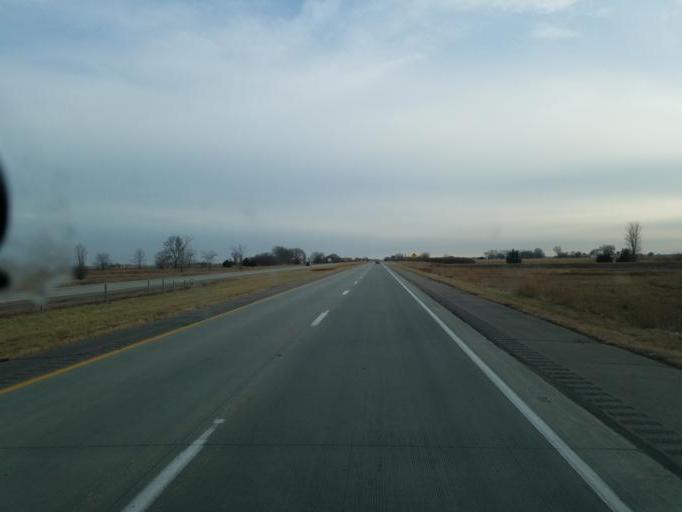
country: US
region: Iowa
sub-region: Monona County
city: Onawa
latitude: 42.1276
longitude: -96.2043
